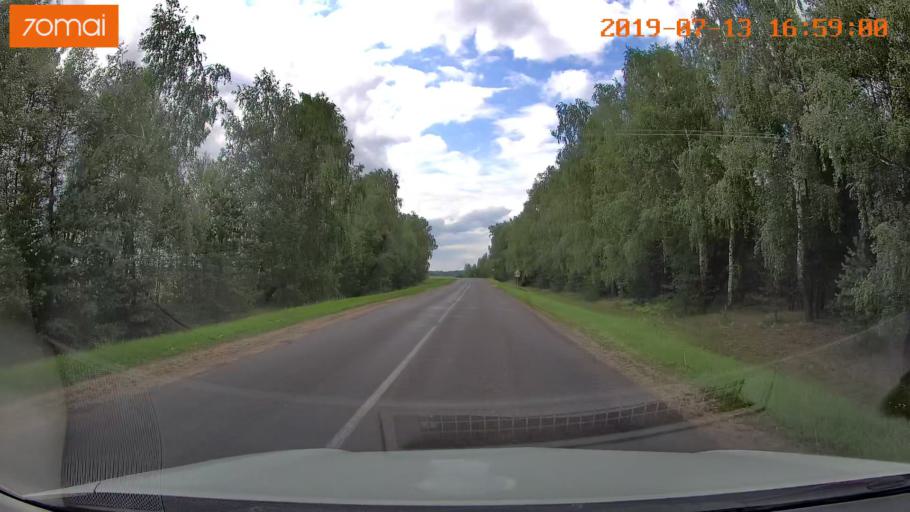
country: BY
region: Mogilev
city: Kirawsk
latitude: 53.2956
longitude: 29.4363
